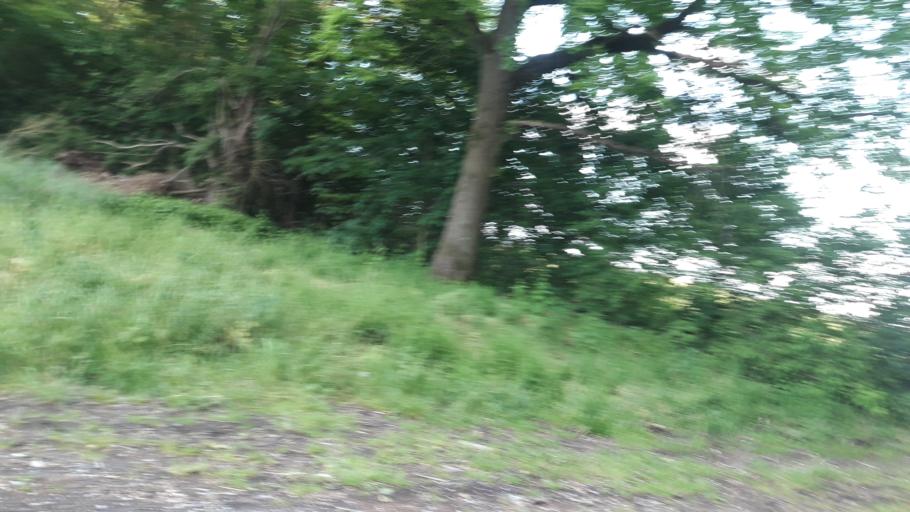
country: DE
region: North Rhine-Westphalia
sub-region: Regierungsbezirk Detmold
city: Paderborn
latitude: 51.6672
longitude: 8.7863
